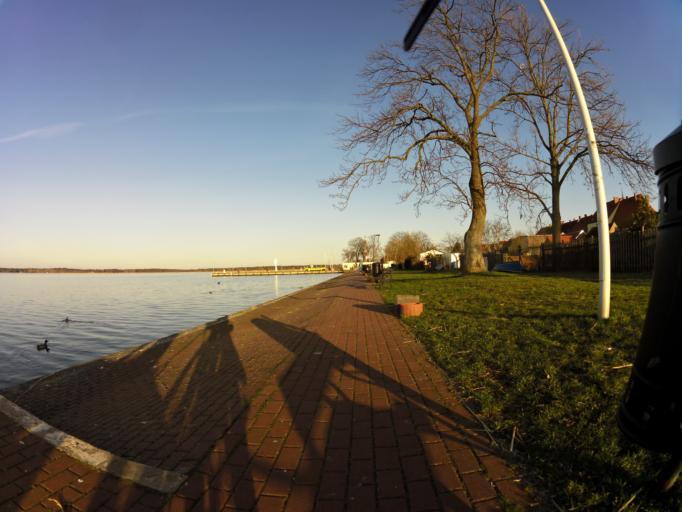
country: PL
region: West Pomeranian Voivodeship
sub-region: Powiat policki
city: Nowe Warpno
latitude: 53.7265
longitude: 14.2798
